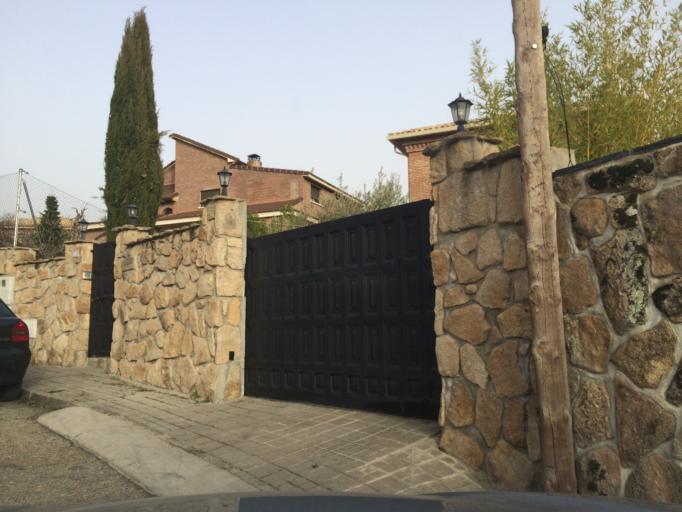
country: ES
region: Madrid
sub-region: Provincia de Madrid
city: Manzanares el Real
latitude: 40.7342
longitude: -3.8617
